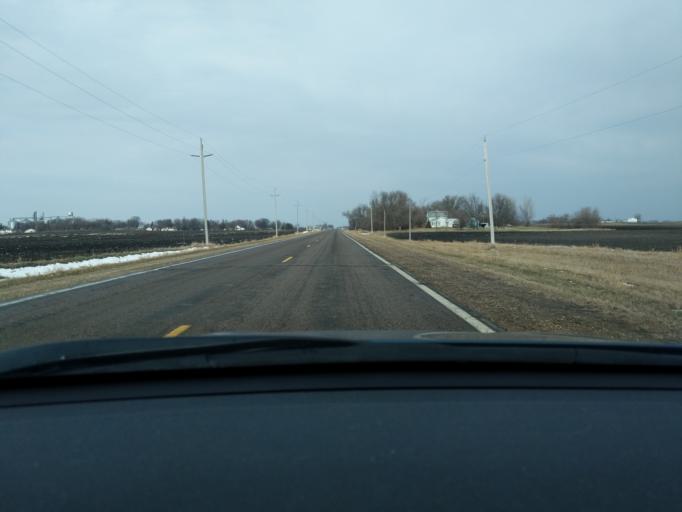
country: US
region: Minnesota
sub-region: Renville County
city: Renville
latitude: 44.7784
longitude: -95.3408
